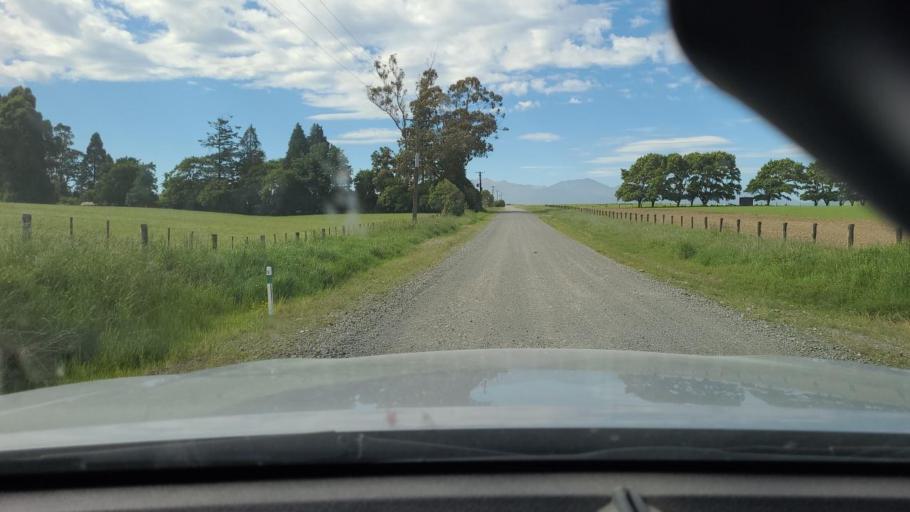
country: NZ
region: Southland
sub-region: Southland District
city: Riverton
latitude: -45.9824
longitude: 167.7603
